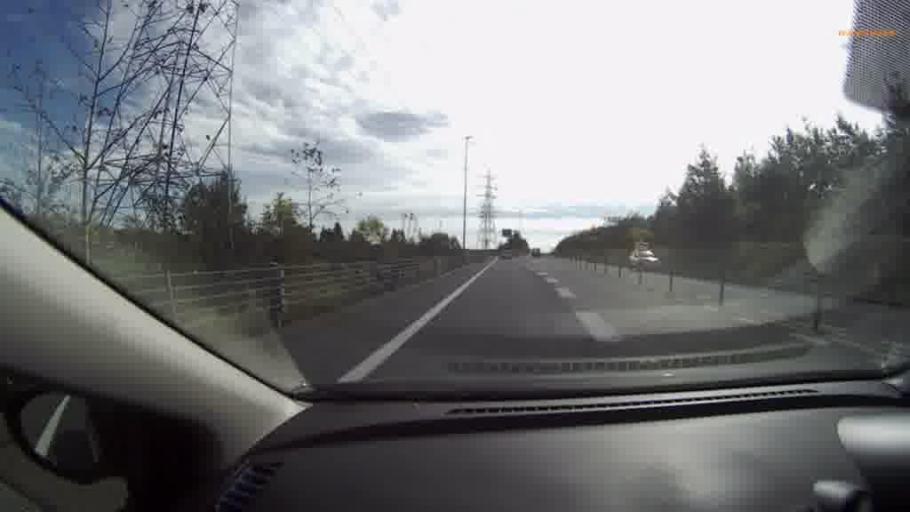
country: JP
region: Hokkaido
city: Kushiro
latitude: 43.0237
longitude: 144.4145
